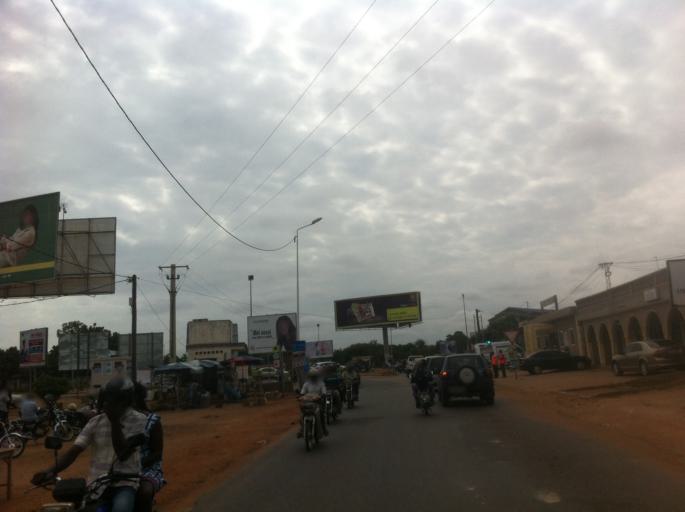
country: TG
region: Maritime
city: Lome
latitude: 6.1886
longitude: 1.1618
